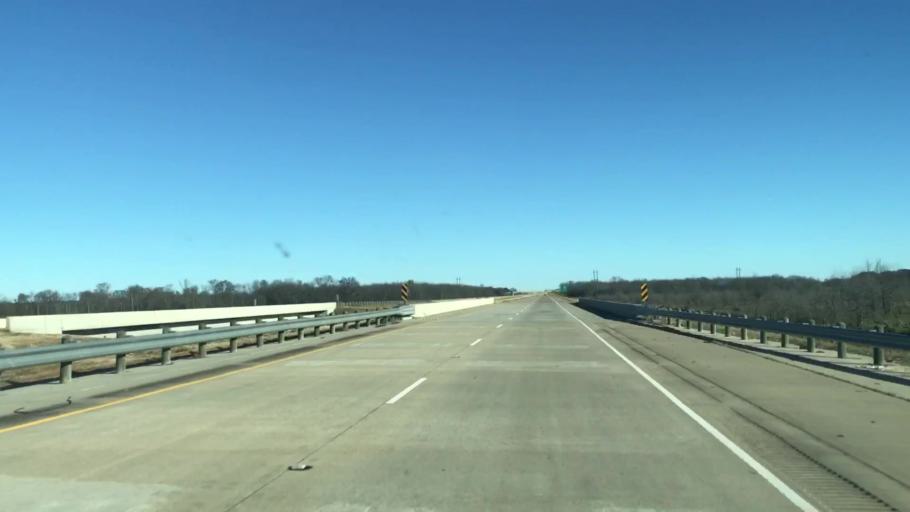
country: US
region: Louisiana
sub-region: Caddo Parish
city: Vivian
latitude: 32.8286
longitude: -93.8758
